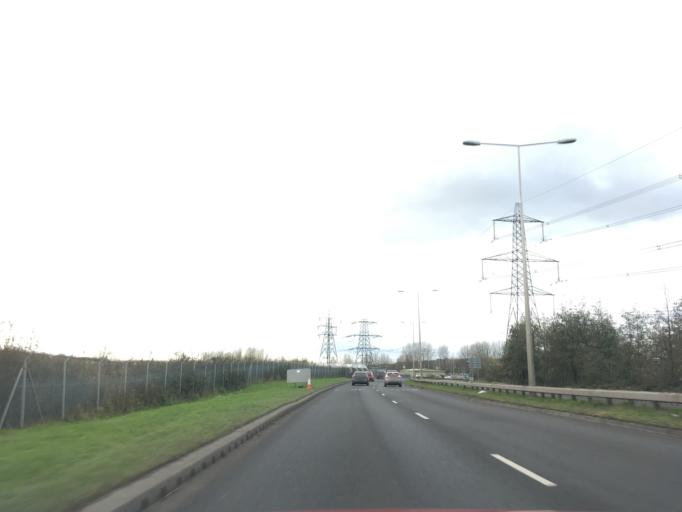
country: GB
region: Wales
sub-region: Newport
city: Newport
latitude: 51.5676
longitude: -2.9986
